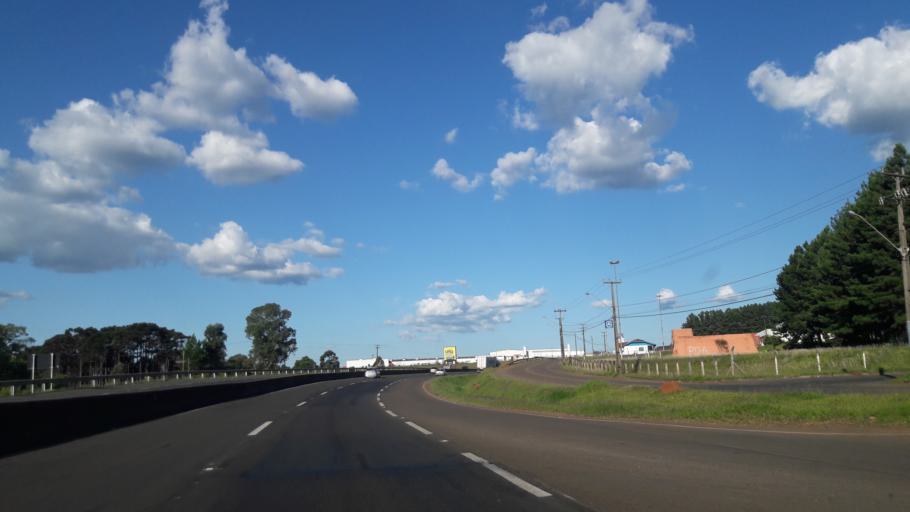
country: BR
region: Parana
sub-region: Guarapuava
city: Guarapuava
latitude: -25.3494
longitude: -51.4559
